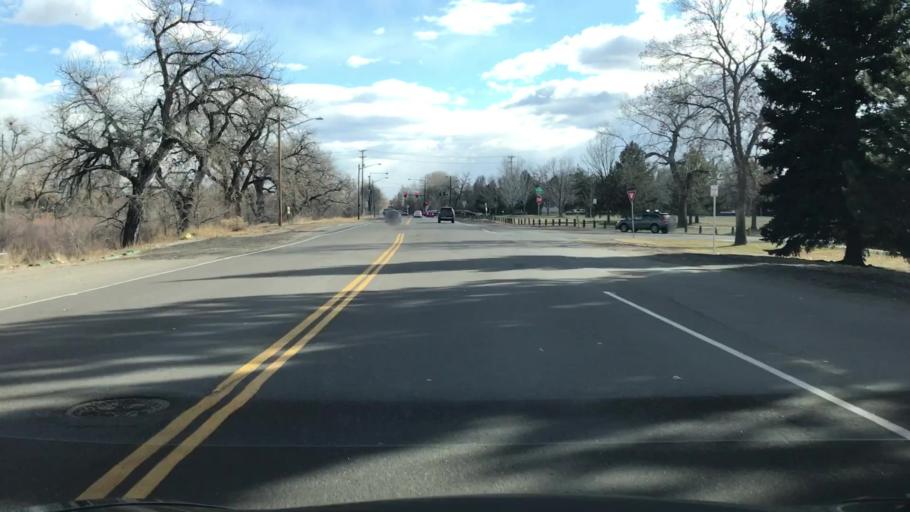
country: US
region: Colorado
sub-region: Arapahoe County
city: Glendale
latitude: 39.6972
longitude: -104.9245
